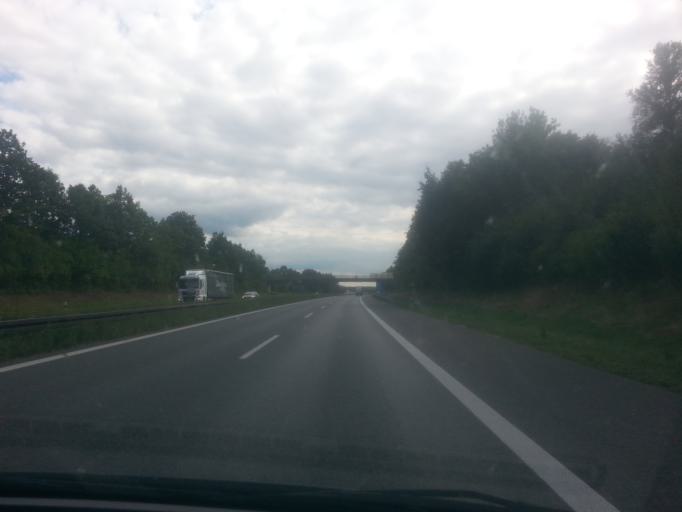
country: DE
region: Bavaria
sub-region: Upper Palatinate
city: Wackersdorf
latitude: 49.3247
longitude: 12.1541
